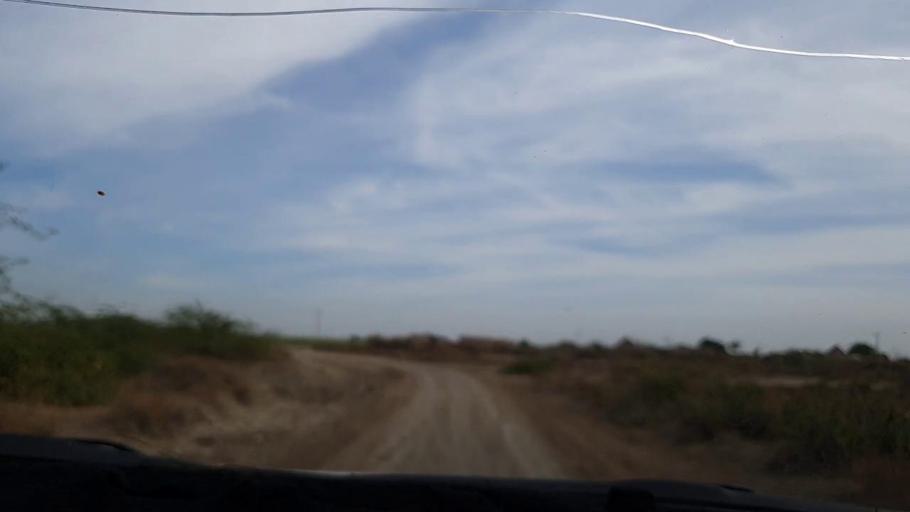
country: PK
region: Sindh
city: Dhoro Naro
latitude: 25.4753
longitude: 69.4784
